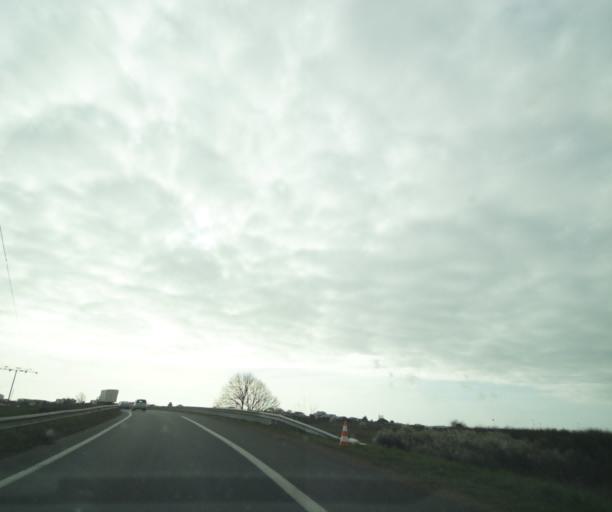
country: FR
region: Poitou-Charentes
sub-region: Departement de la Charente-Maritime
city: Lagord
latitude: 46.1720
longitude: -1.1887
